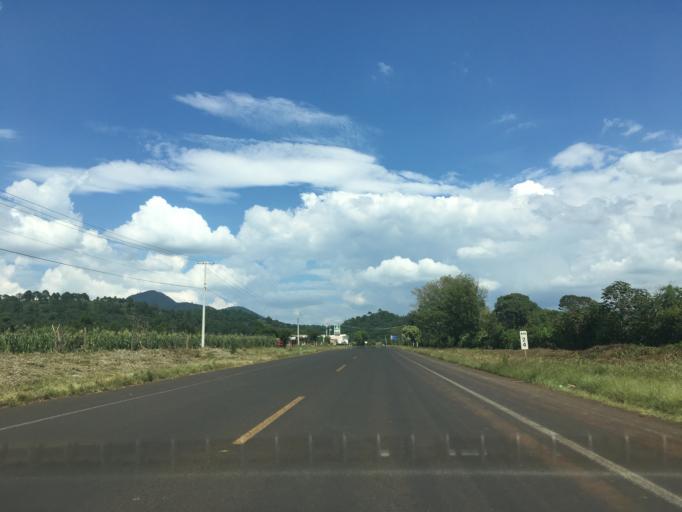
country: MX
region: Michoacan
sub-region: Tingueindin
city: Tingueindin
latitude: 19.8424
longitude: -102.4825
